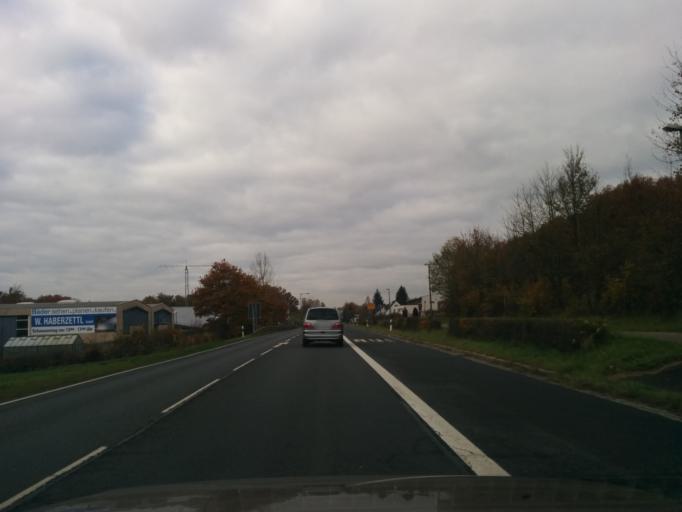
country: DE
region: Bavaria
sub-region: Regierungsbezirk Mittelfranken
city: Uttenreuth
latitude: 49.5958
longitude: 11.0847
